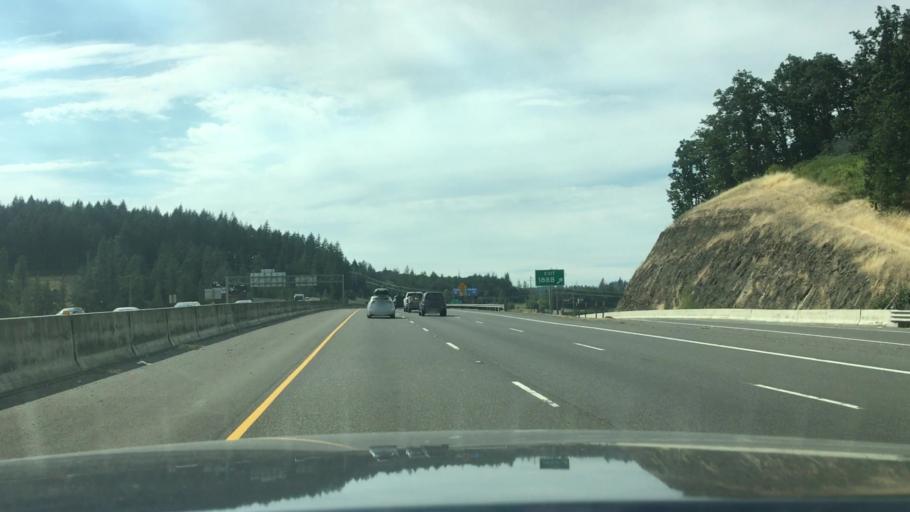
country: US
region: Oregon
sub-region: Lane County
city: Springfield
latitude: 44.0001
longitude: -123.0125
